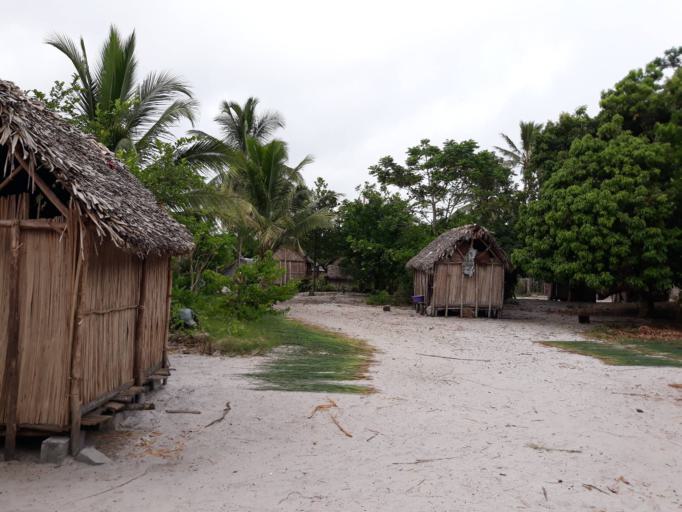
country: MG
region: Atsinanana
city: Andovoranto
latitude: -19.2561
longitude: 48.9744
